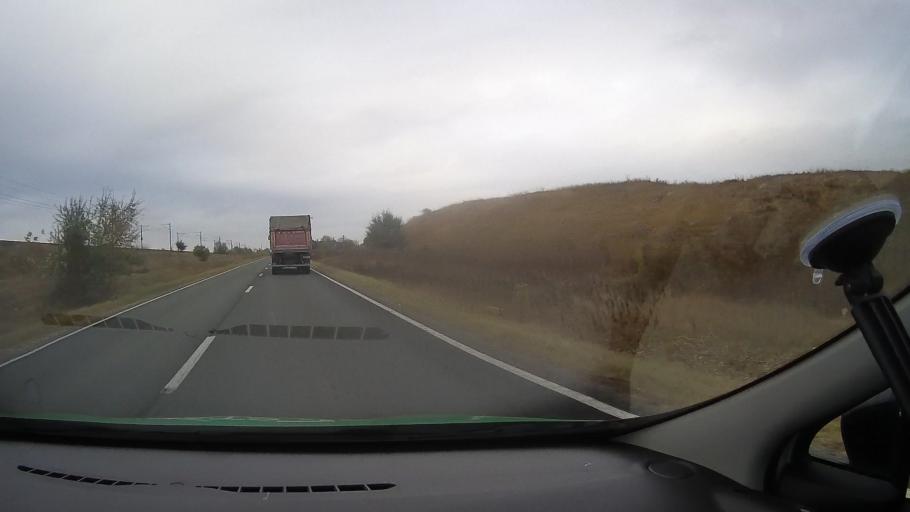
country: RO
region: Constanta
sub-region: Comuna Poarta Alba
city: Poarta Alba
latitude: 44.2243
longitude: 28.3845
